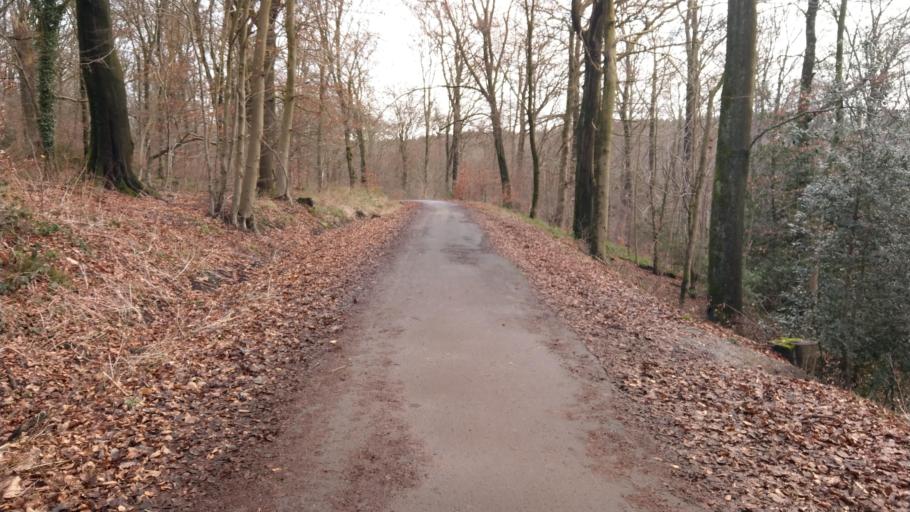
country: DE
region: North Rhine-Westphalia
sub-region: Regierungsbezirk Koln
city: Aachen
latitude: 50.7381
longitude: 6.0613
